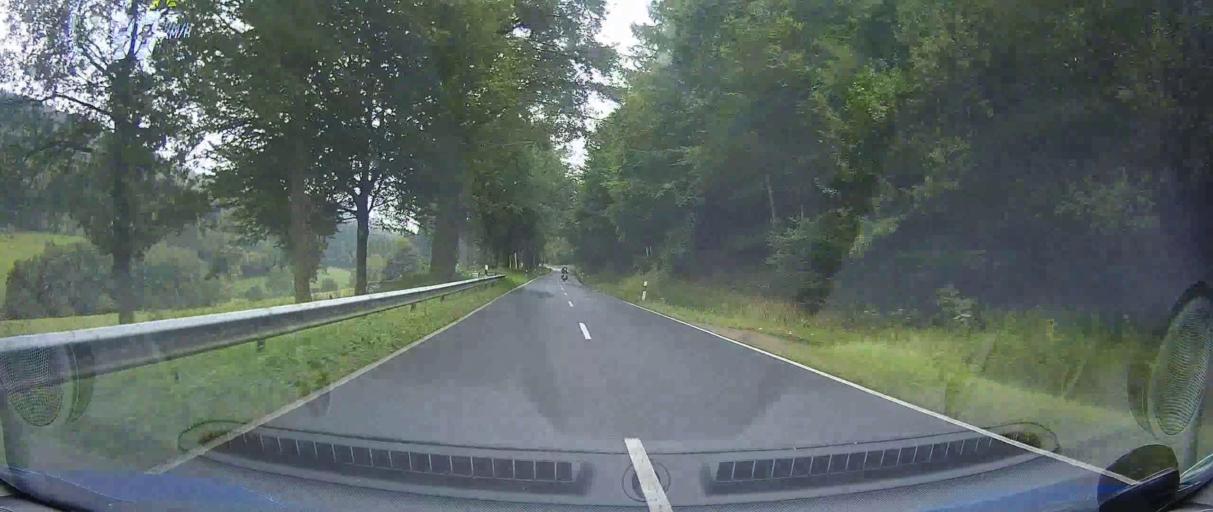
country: DE
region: Lower Saxony
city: Uslar
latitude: 51.6969
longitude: 9.6276
